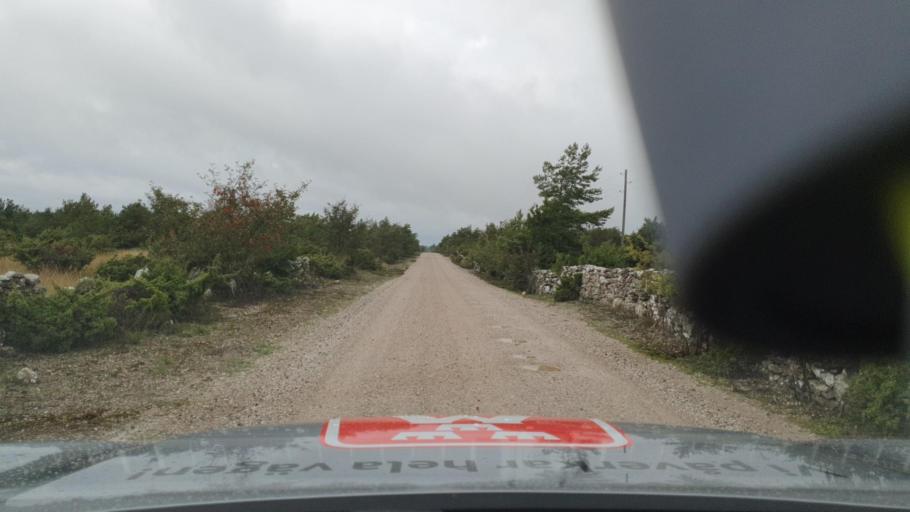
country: SE
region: Gotland
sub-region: Gotland
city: Hemse
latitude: 56.9411
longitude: 18.2280
